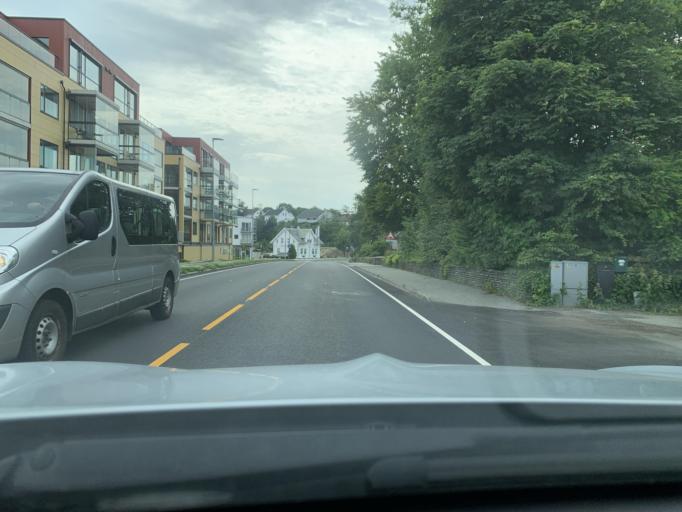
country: NO
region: Rogaland
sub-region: Sandnes
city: Sandnes
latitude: 58.7798
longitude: 5.7199
